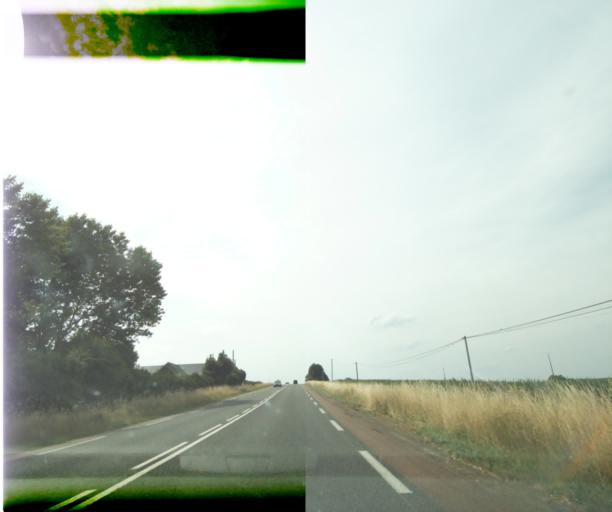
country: FR
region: Pays de la Loire
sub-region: Departement de la Sarthe
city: Luceau
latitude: 47.7422
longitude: 0.3849
